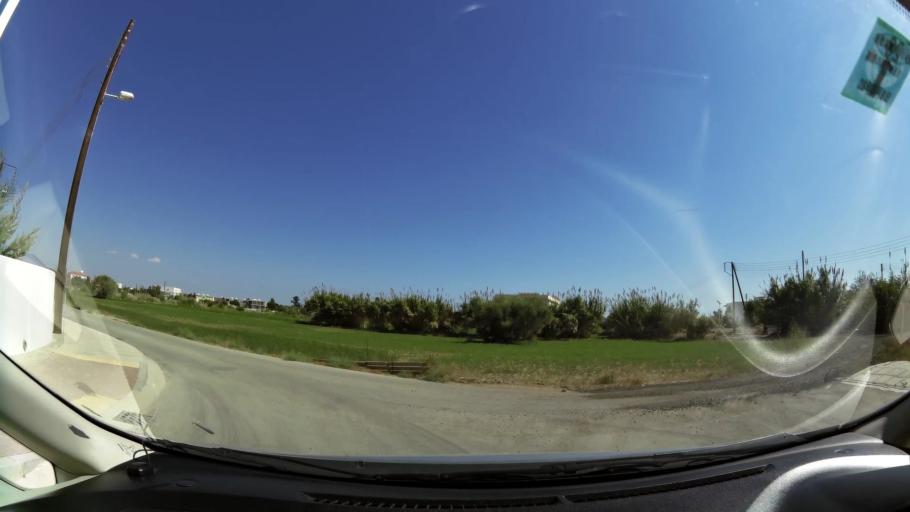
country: CY
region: Larnaka
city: Livadia
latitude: 34.9566
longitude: 33.6309
